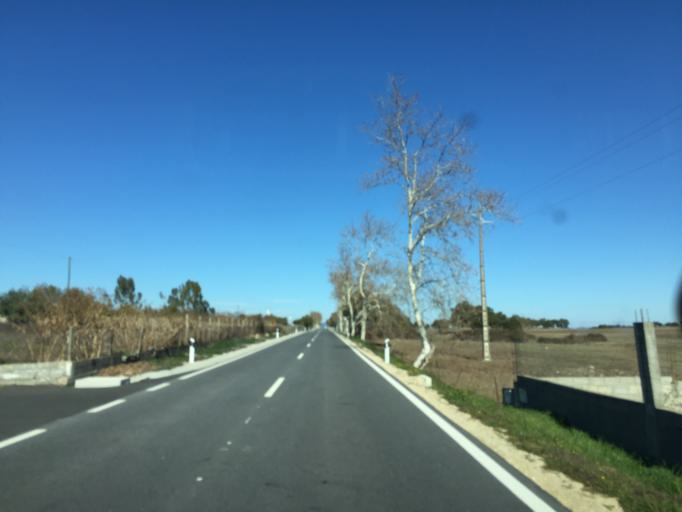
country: PT
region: Guarda
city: Alcains
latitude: 39.9407
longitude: -7.4571
